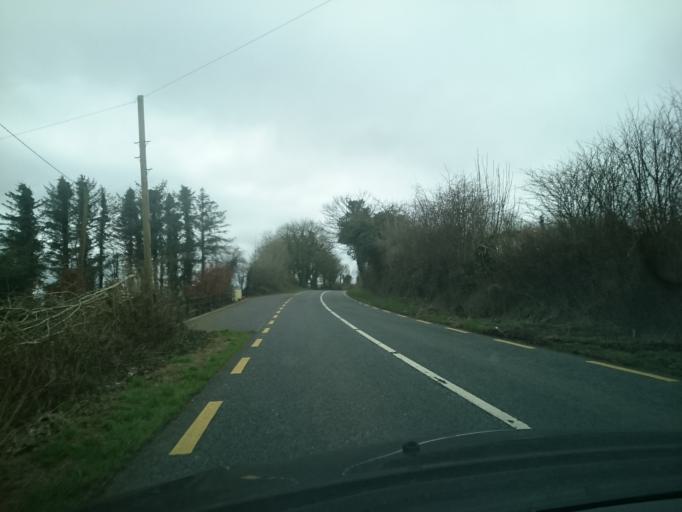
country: IE
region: Connaught
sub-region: Maigh Eo
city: Ballyhaunis
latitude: 53.7322
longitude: -8.8610
